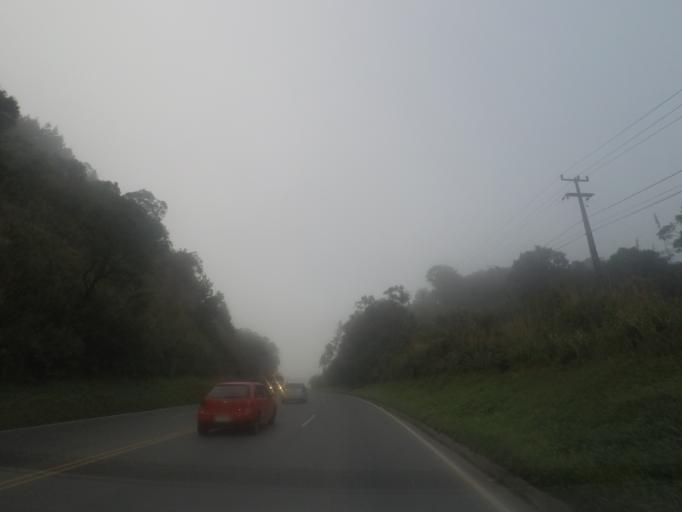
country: BR
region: Parana
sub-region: Almirante Tamandare
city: Almirante Tamandare
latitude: -25.2765
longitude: -49.3036
